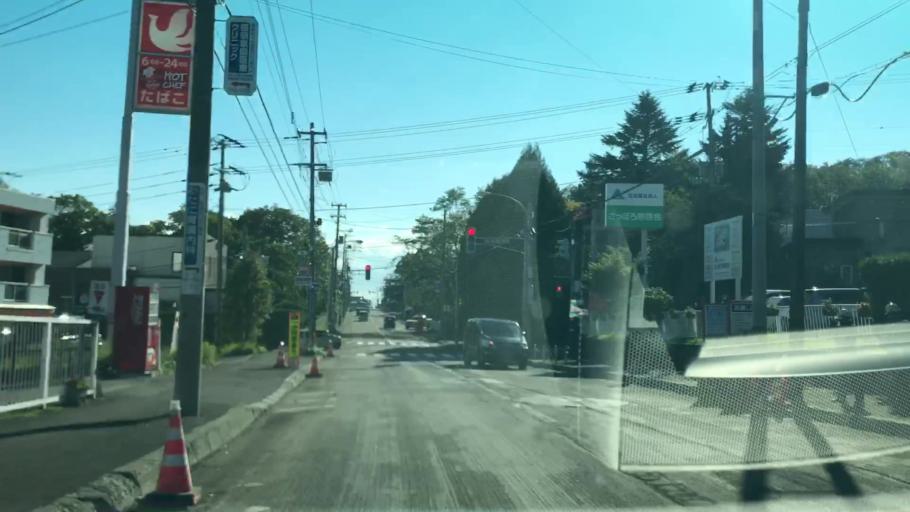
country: JP
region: Hokkaido
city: Sapporo
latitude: 43.0380
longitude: 141.3232
